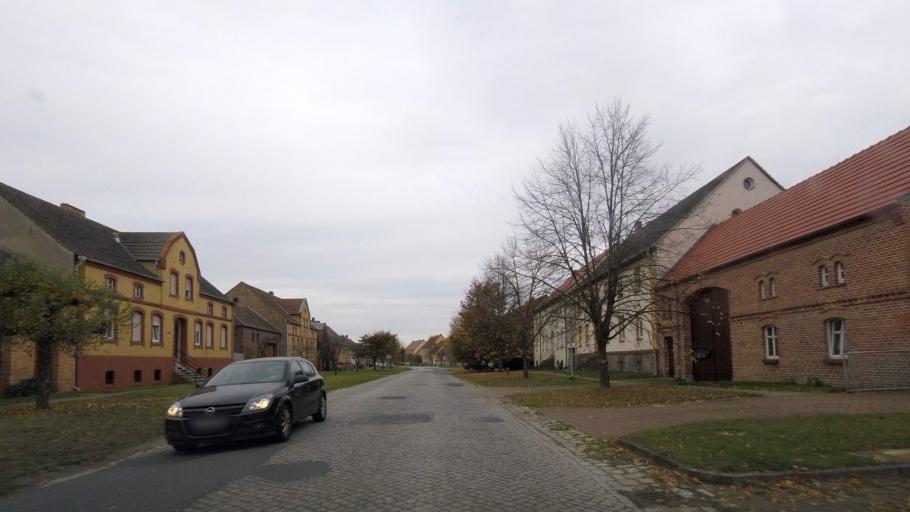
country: DE
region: Brandenburg
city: Treuenbrietzen
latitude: 52.0729
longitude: 12.9419
